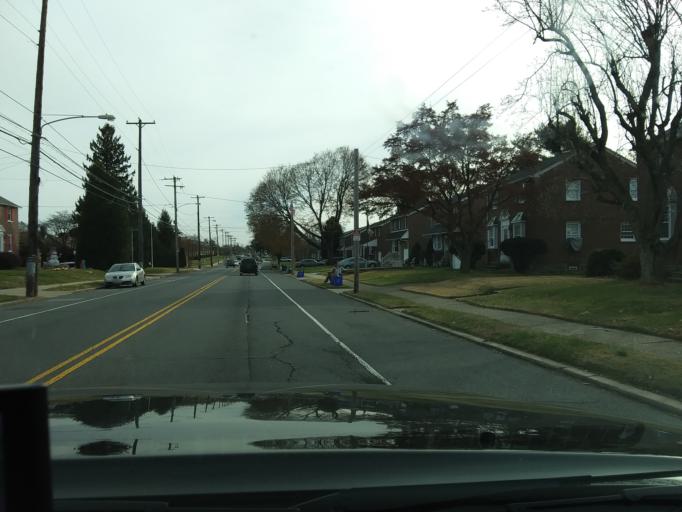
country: US
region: Pennsylvania
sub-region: Montgomery County
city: Rockledge
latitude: 40.0710
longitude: -75.0721
